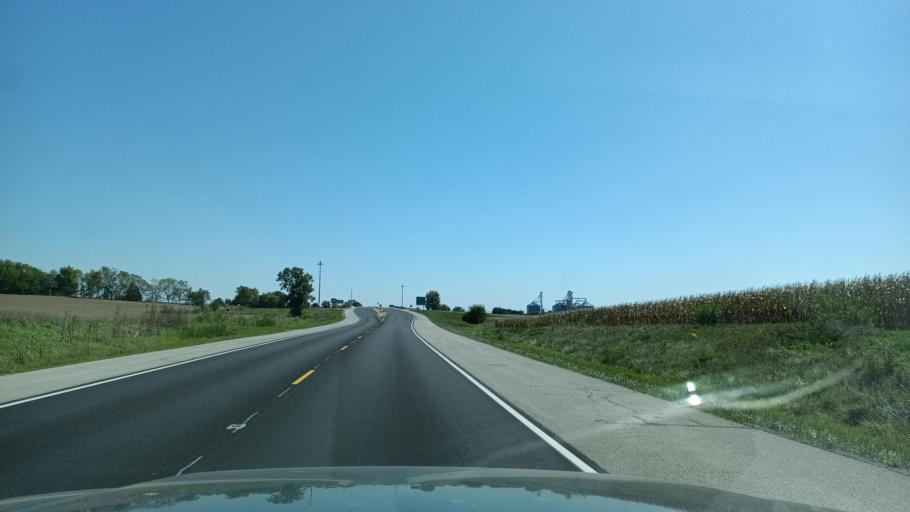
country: US
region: Illinois
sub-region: McLean County
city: Twin Grove
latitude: 40.5434
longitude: -89.0665
